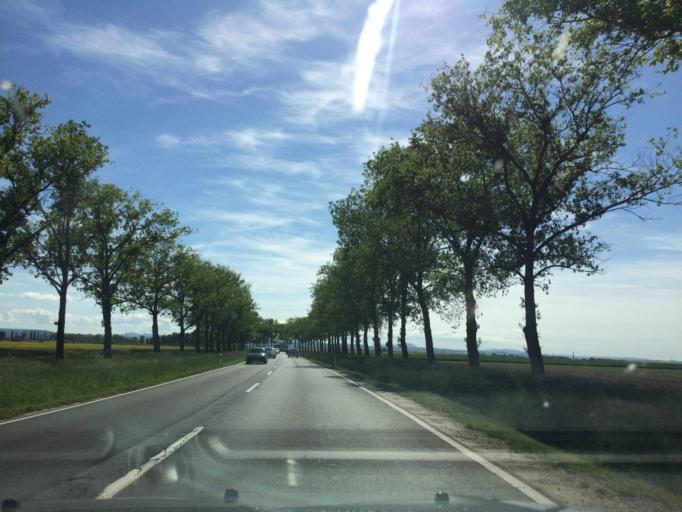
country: PL
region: Lower Silesian Voivodeship
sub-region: Powiat swidnicki
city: Swidnica
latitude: 50.8728
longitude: 16.5696
